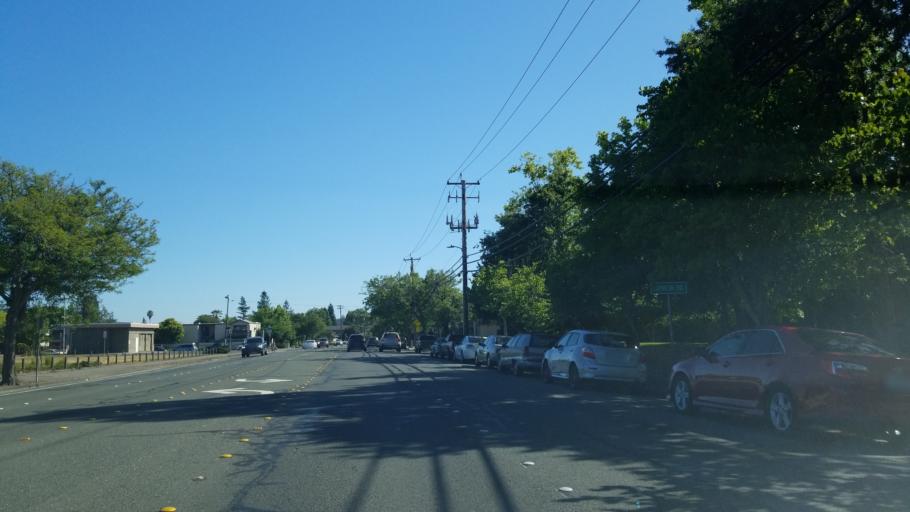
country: US
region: California
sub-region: Sonoma County
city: Santa Rosa
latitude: 38.4745
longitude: -122.6750
